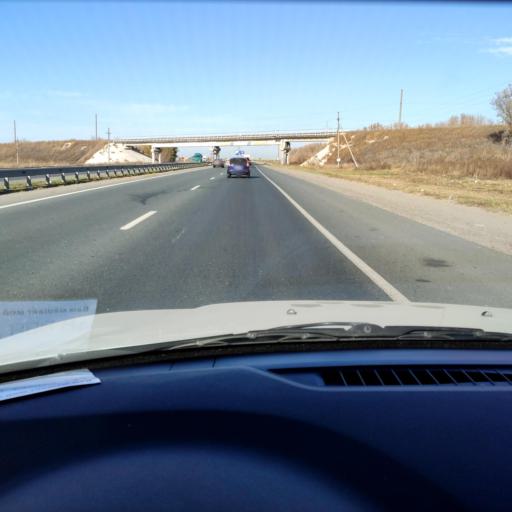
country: RU
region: Samara
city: Tol'yatti
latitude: 53.5618
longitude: 49.4984
